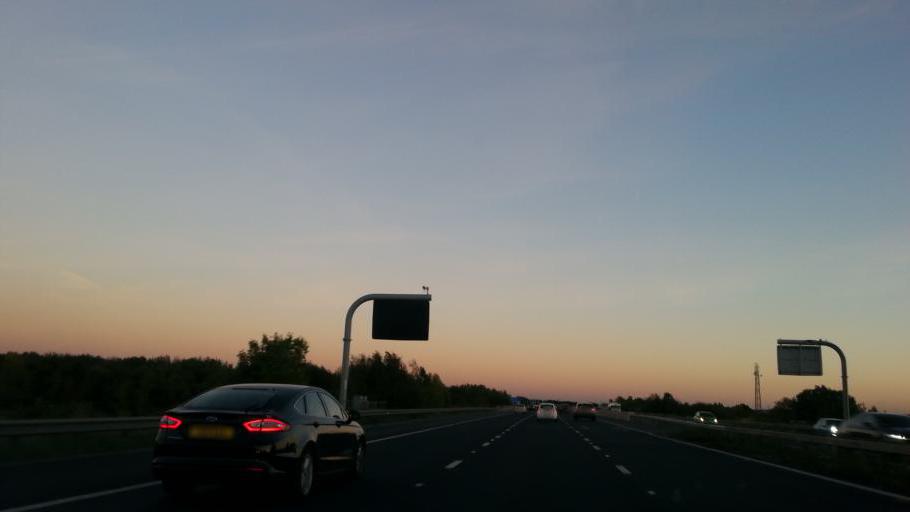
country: GB
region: England
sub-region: City and Borough of Wakefield
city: Normanton
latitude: 53.7210
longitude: -1.4274
